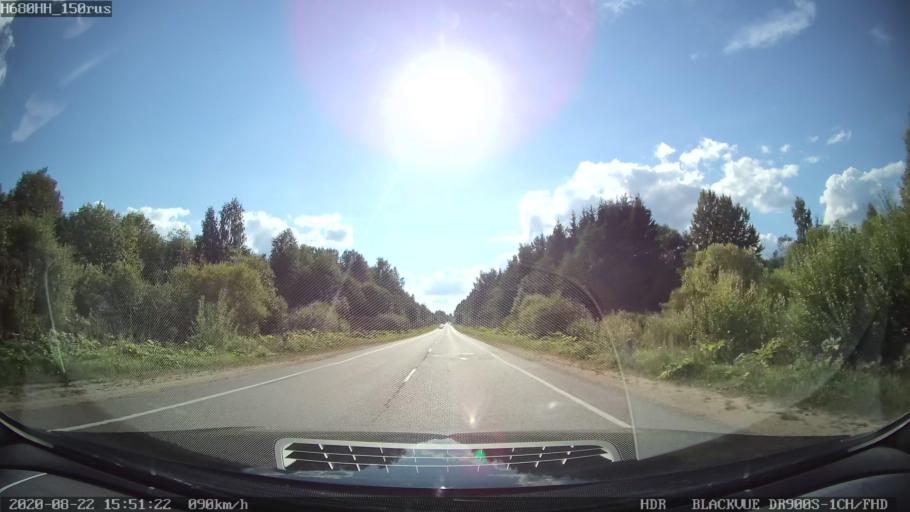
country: RU
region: Tverskaya
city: Bezhetsk
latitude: 57.6652
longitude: 36.4272
